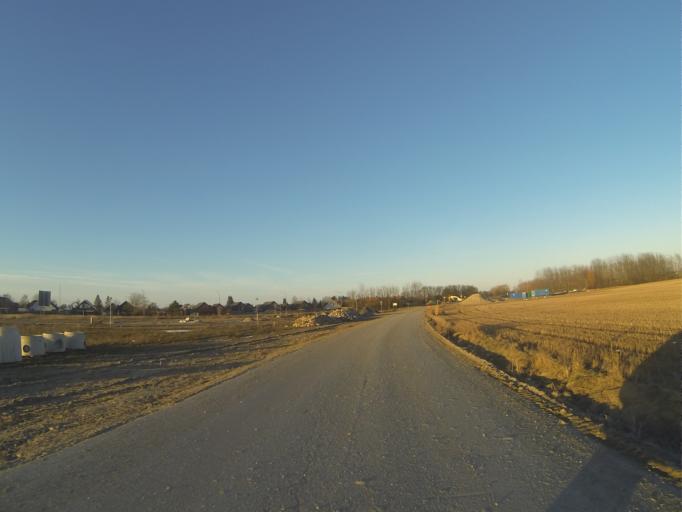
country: SE
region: Skane
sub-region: Staffanstorps Kommun
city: Staffanstorp
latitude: 55.6316
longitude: 13.2057
